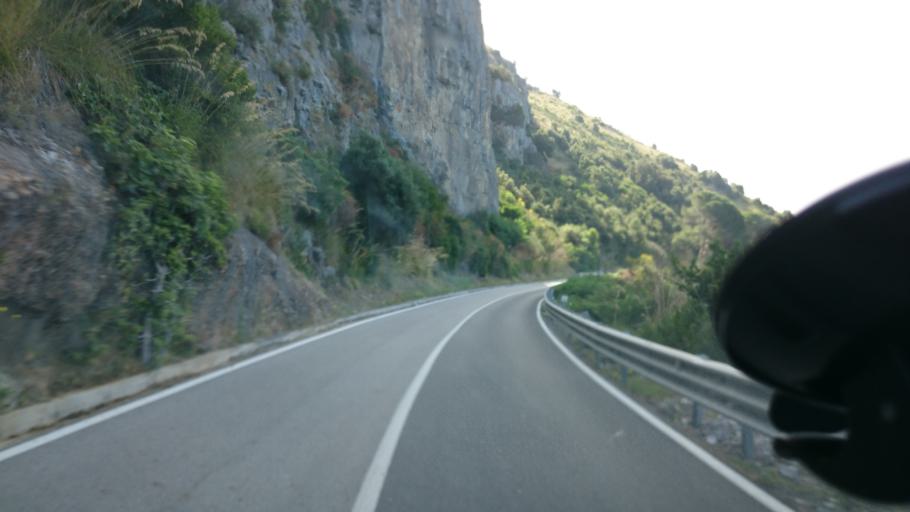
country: IT
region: Campania
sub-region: Provincia di Salerno
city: Sapri
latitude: 40.0503
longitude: 15.6377
